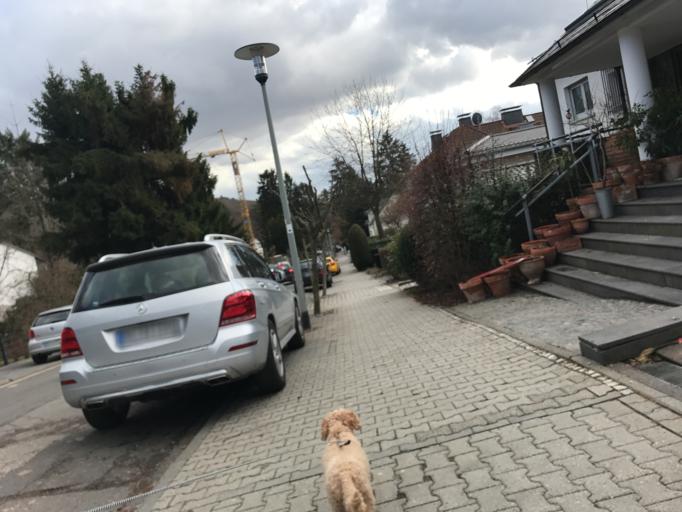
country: DE
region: Hesse
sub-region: Regierungsbezirk Darmstadt
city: Konigstein im Taunus
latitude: 50.1937
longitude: 8.4674
